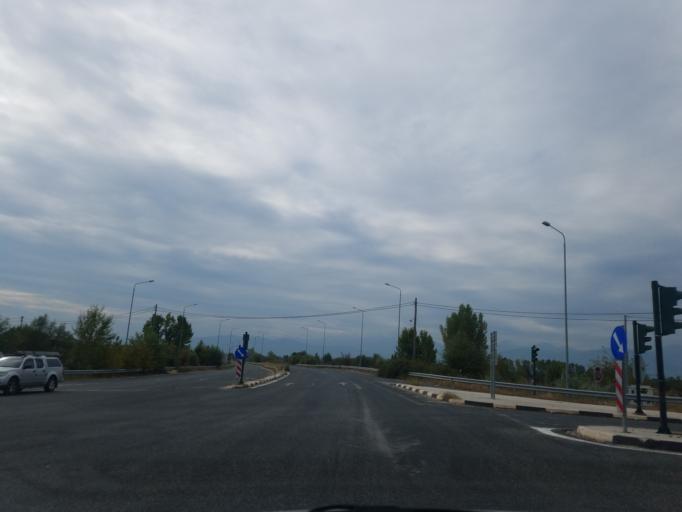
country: GR
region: Thessaly
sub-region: Trikala
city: Pyrgetos
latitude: 39.5581
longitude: 21.7340
